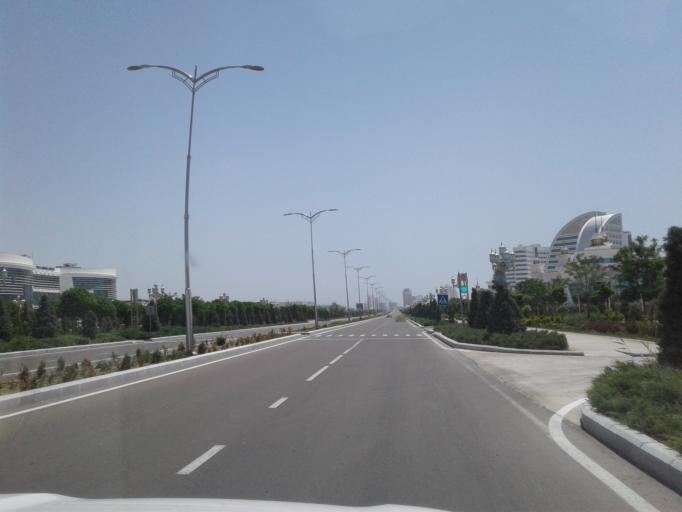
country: TM
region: Balkan
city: Turkmenbasy
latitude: 39.9793
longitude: 52.8274
